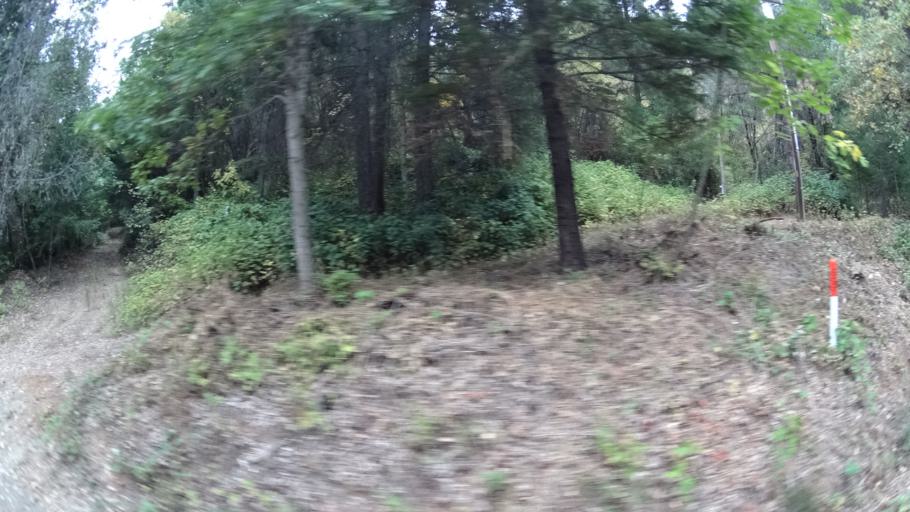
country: US
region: California
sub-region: Siskiyou County
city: Happy Camp
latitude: 41.7935
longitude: -123.3428
